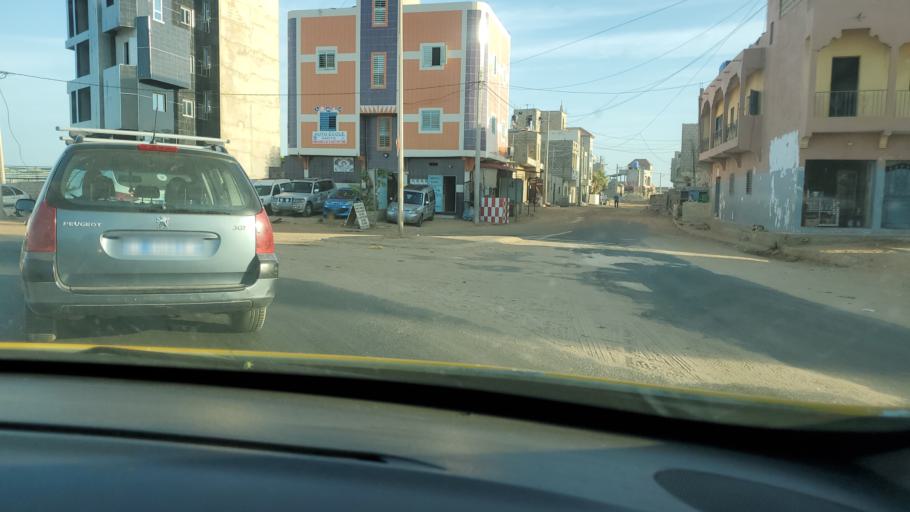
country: SN
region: Dakar
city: Pikine
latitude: 14.8125
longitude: -17.2877
